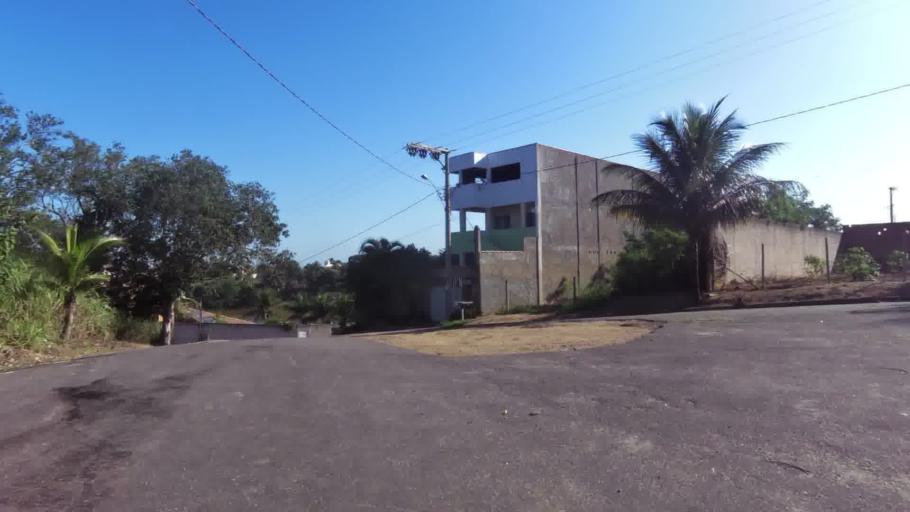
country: BR
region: Espirito Santo
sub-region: Guarapari
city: Guarapari
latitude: -20.7463
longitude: -40.5590
